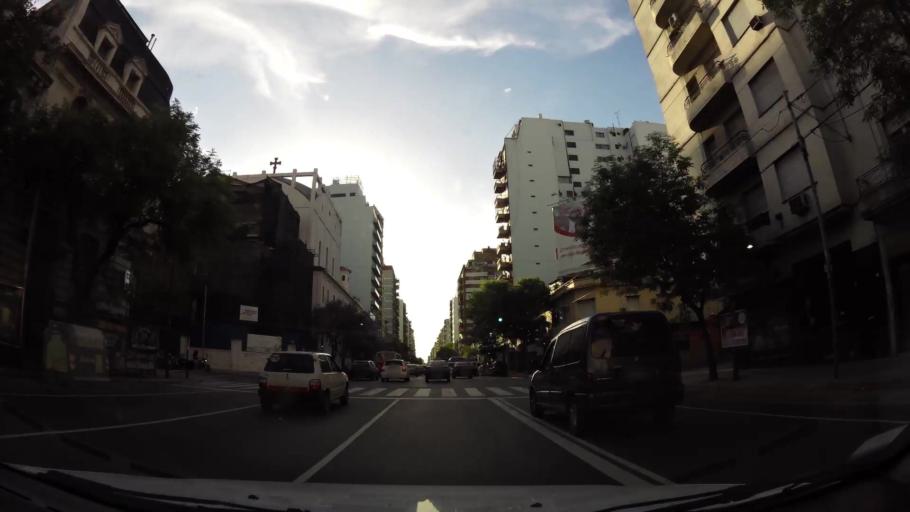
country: AR
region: Buenos Aires F.D.
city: Retiro
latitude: -34.5981
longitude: -58.4117
